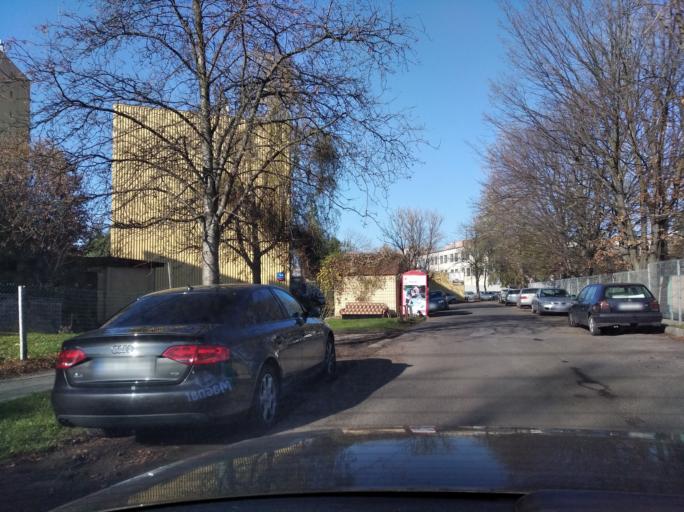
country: PL
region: Subcarpathian Voivodeship
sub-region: Rzeszow
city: Rzeszow
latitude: 50.0319
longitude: 21.9900
